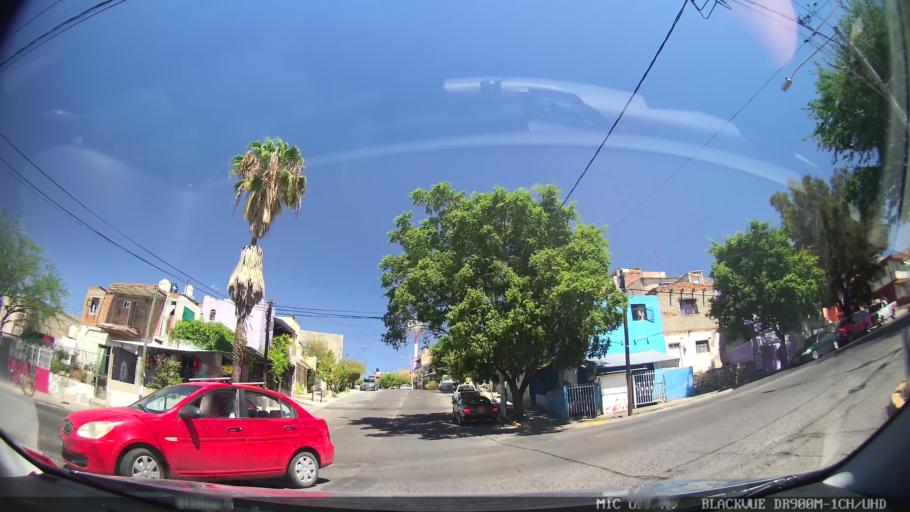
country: MX
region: Jalisco
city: Tlaquepaque
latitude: 20.6945
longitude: -103.2913
